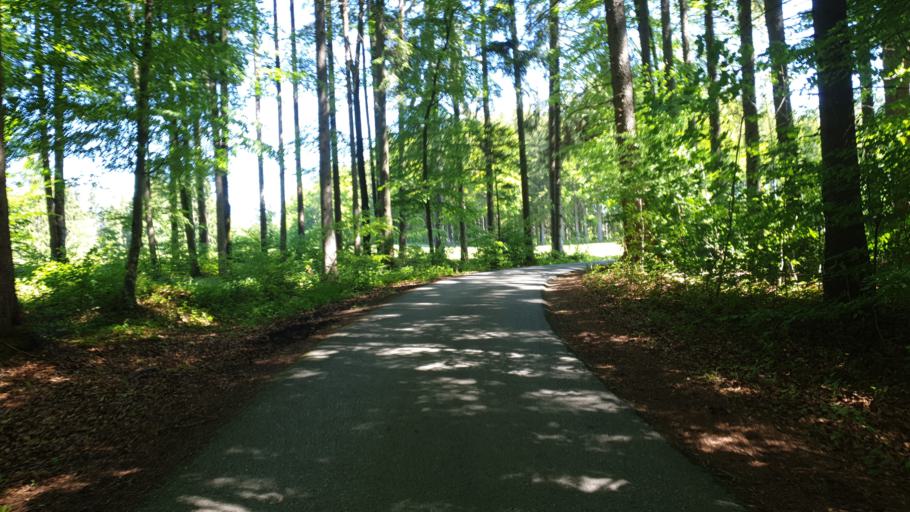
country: DE
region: Bavaria
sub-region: Upper Bavaria
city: Habach
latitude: 47.7548
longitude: 11.2600
